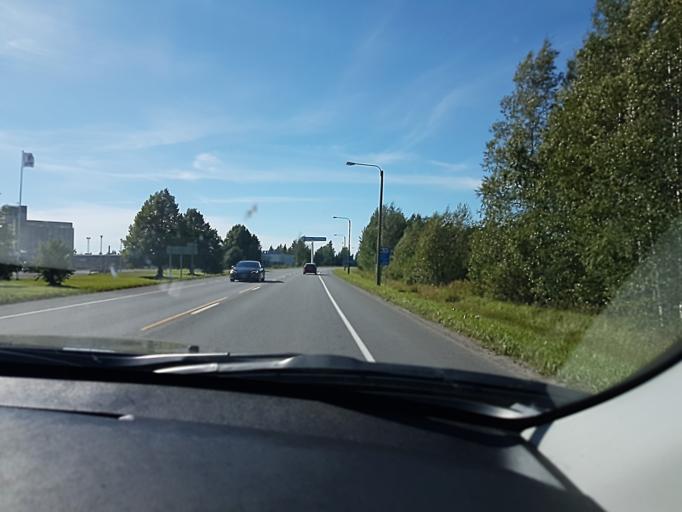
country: FI
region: Southern Ostrobothnia
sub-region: Seinaejoki
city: Nurmo
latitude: 62.7914
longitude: 22.8866
